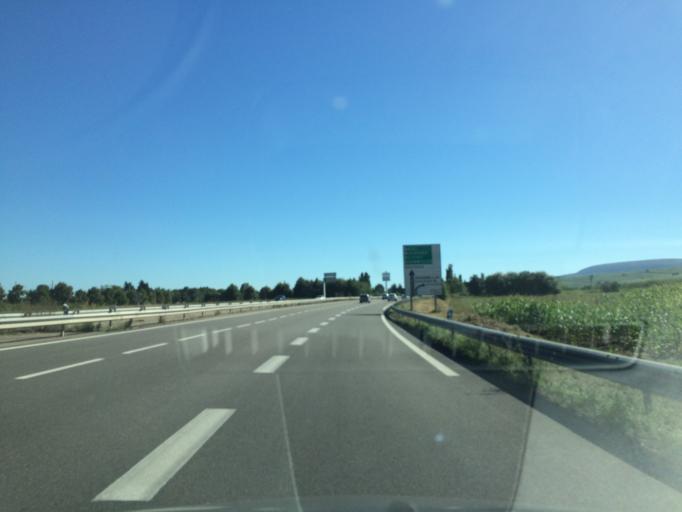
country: FR
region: Alsace
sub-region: Departement du Haut-Rhin
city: Eguisheim
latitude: 48.0442
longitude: 7.3236
